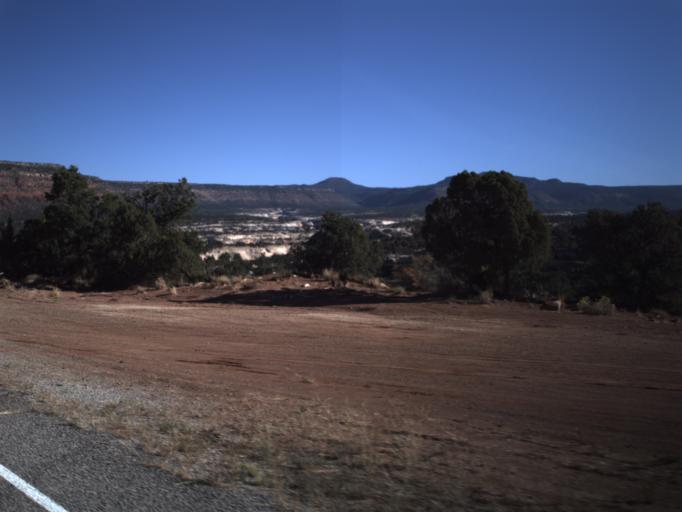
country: US
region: Utah
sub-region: San Juan County
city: Blanding
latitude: 37.5822
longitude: -110.0396
